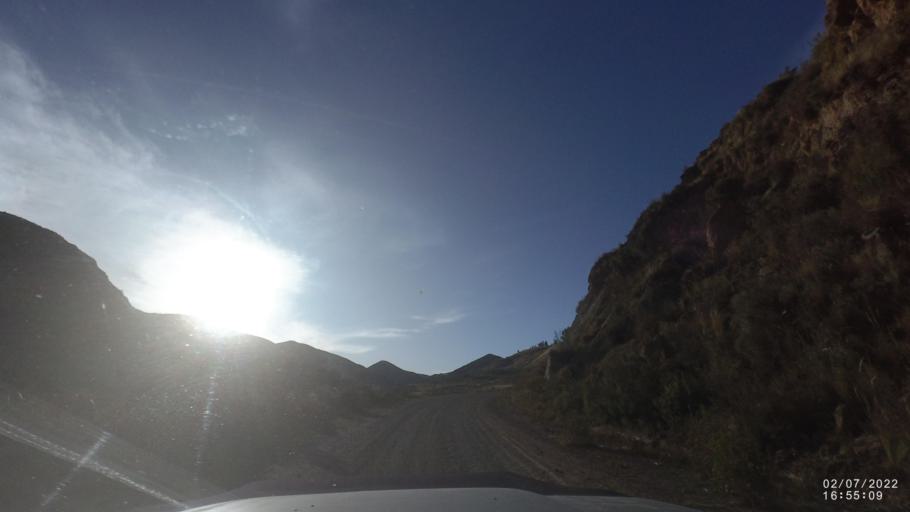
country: BO
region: Cochabamba
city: Irpa Irpa
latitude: -17.9624
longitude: -66.5405
